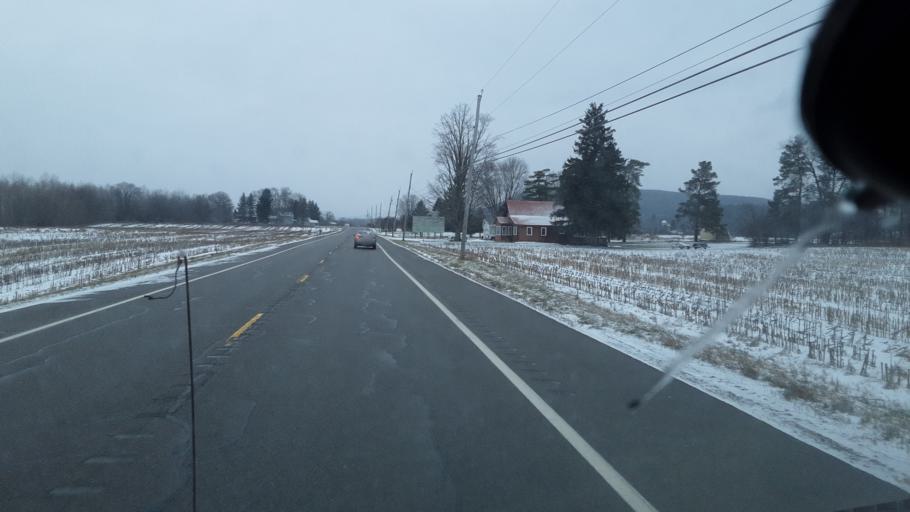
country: US
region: New York
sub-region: Allegany County
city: Belmont
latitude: 42.1902
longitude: -77.9887
